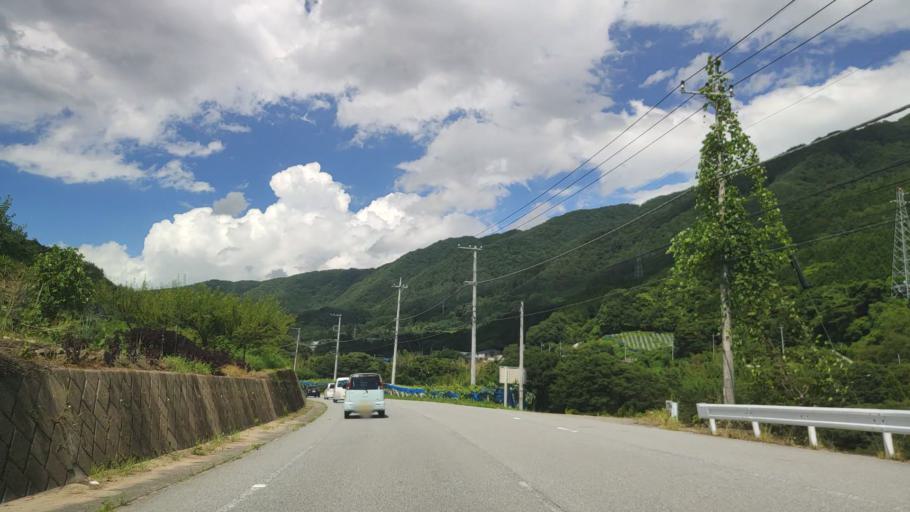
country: JP
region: Yamanashi
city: Enzan
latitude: 35.7599
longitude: 138.7316
